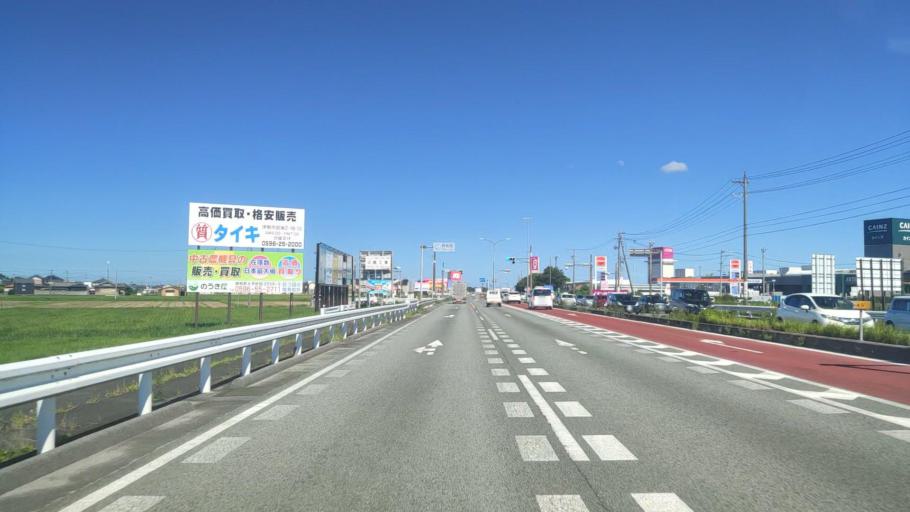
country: JP
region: Mie
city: Ise
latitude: 34.5841
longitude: 136.6114
